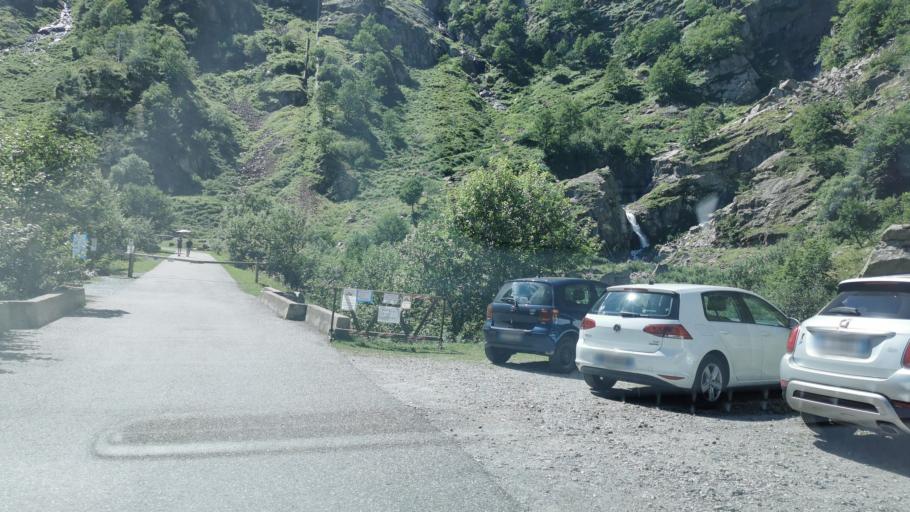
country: IT
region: Piedmont
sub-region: Provincia di Cuneo
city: Entracque
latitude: 44.1741
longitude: 7.3402
